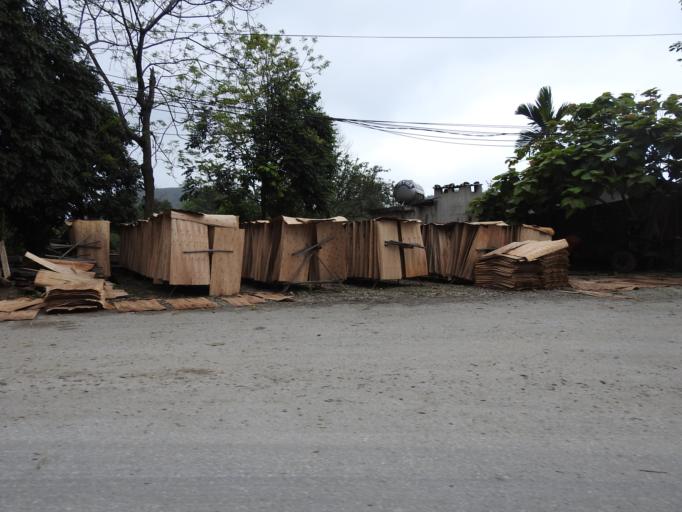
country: VN
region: Yen Bai
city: Yen Bai
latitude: 21.7938
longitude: 104.9157
